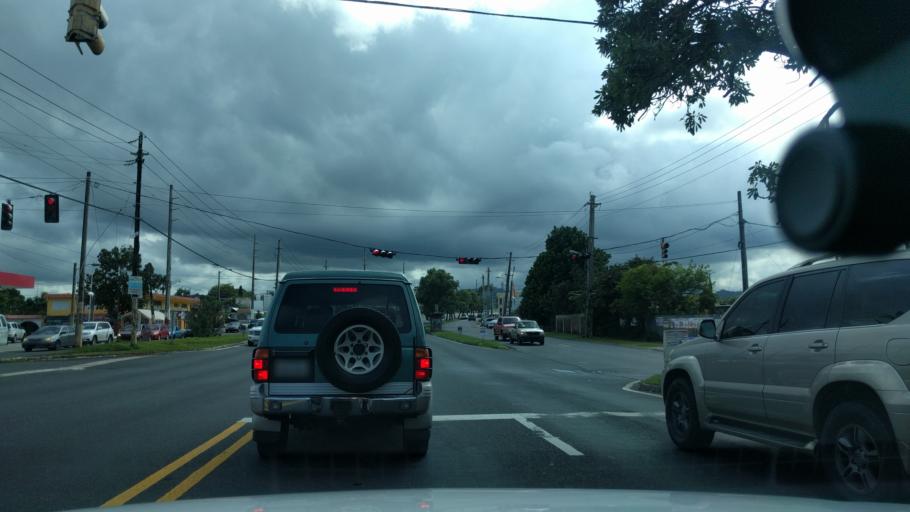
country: PR
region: Toa Alta
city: Pajaros
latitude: 18.3520
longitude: -66.1887
